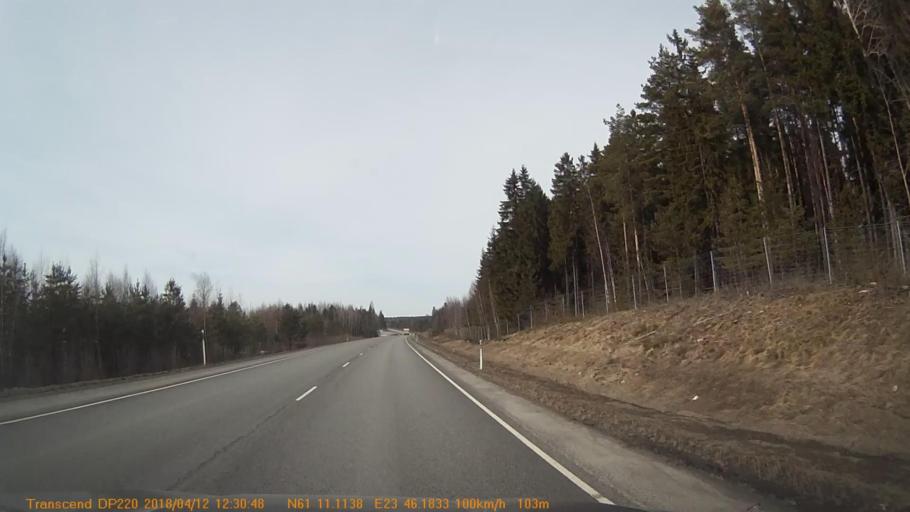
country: FI
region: Pirkanmaa
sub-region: Etelae-Pirkanmaa
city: Viiala
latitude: 61.1854
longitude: 23.7688
